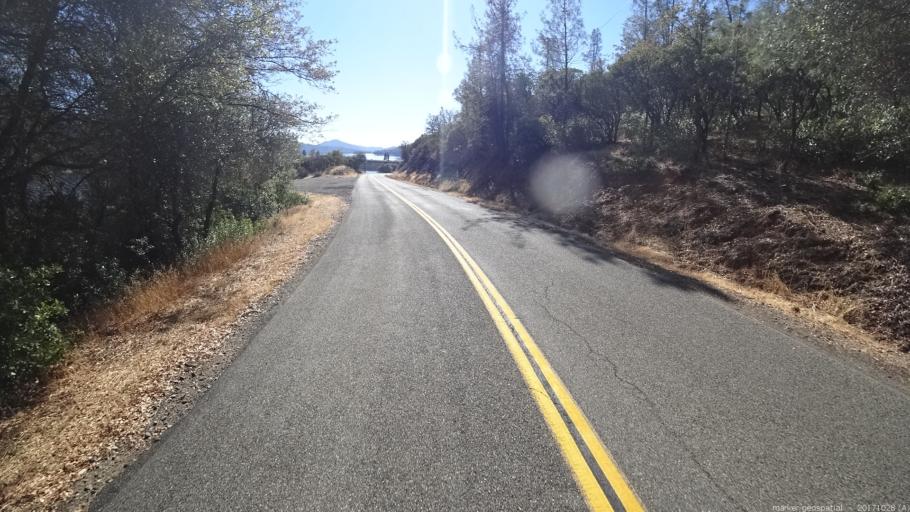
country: US
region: California
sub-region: Shasta County
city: Shasta
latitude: 40.6376
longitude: -122.5601
